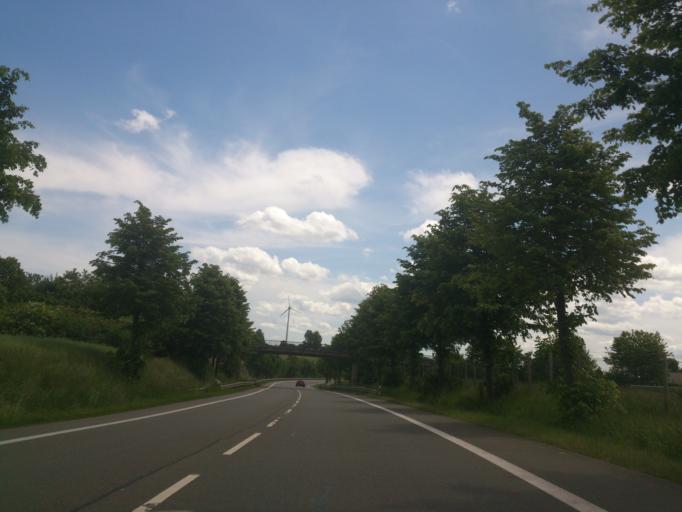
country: DE
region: North Rhine-Westphalia
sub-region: Regierungsbezirk Detmold
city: Willebadessen
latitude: 51.6039
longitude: 9.1354
